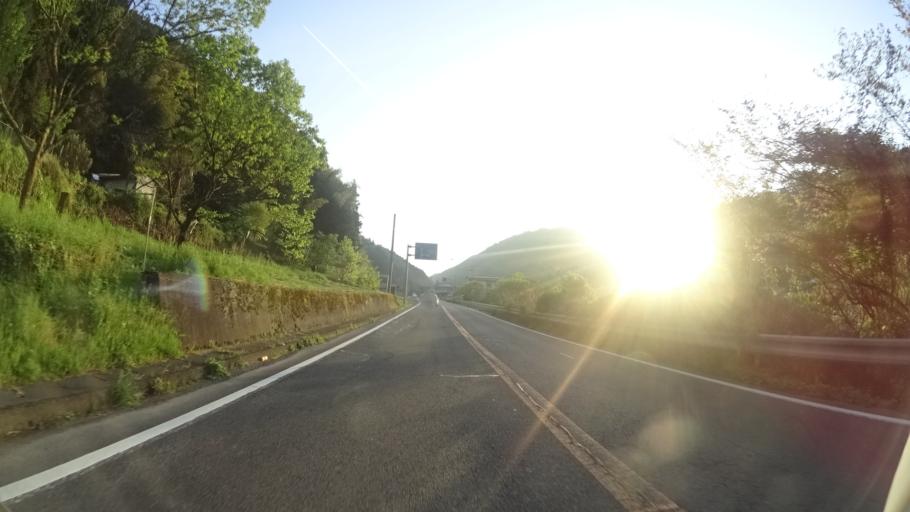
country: JP
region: Tokushima
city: Ikedacho
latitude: 34.0031
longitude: 133.7090
